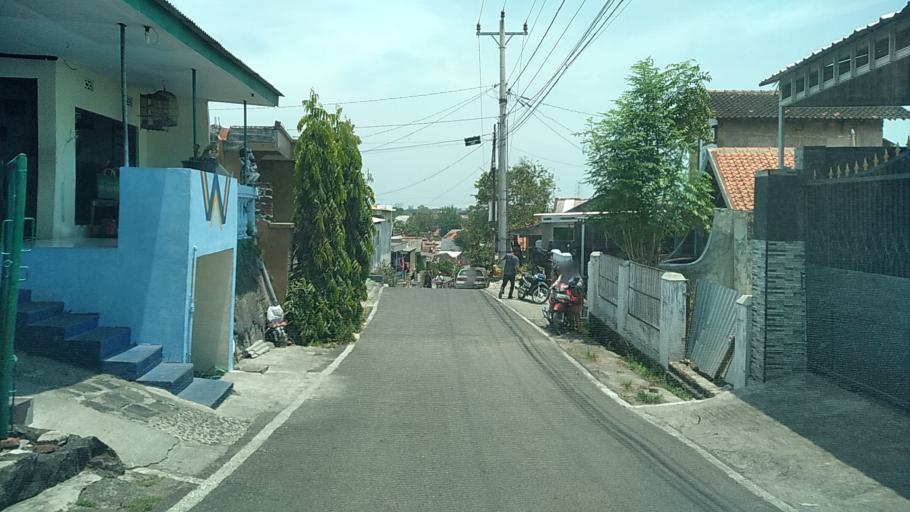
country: ID
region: Central Java
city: Semarang
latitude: -7.0098
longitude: 110.4495
